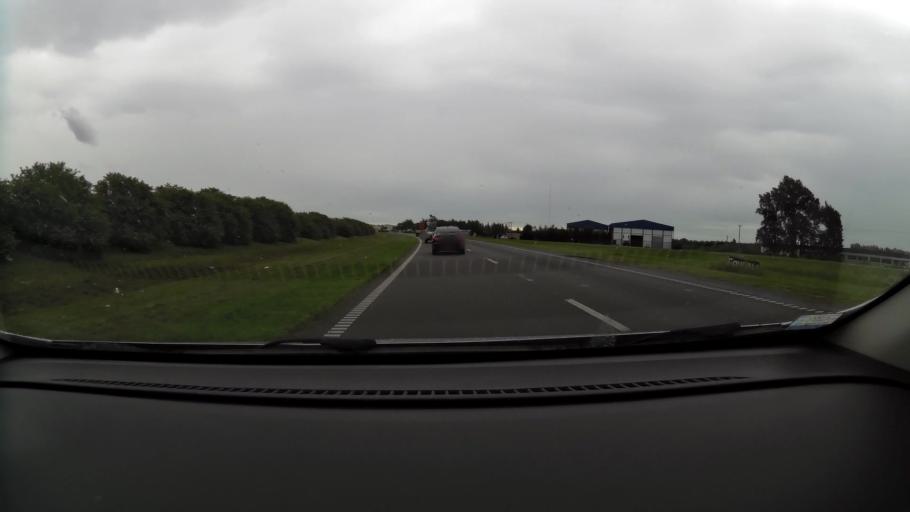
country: AR
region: Buenos Aires
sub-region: Partido de San Pedro
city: San Pedro
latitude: -33.7757
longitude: -59.6527
